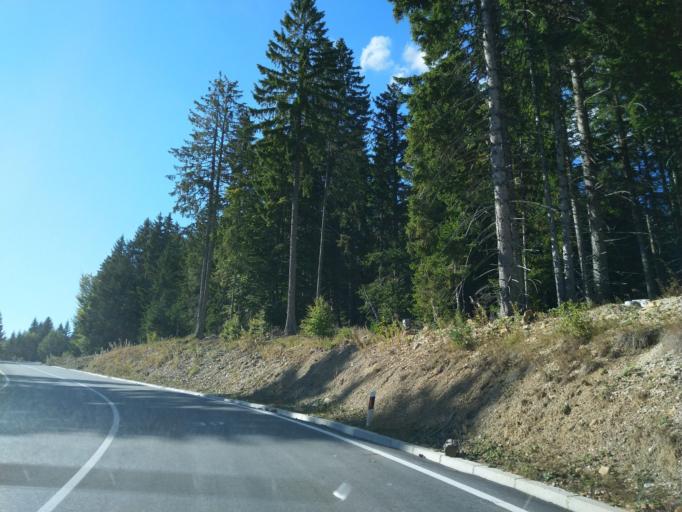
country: RS
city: Sokolovica
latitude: 43.3026
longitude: 20.3089
